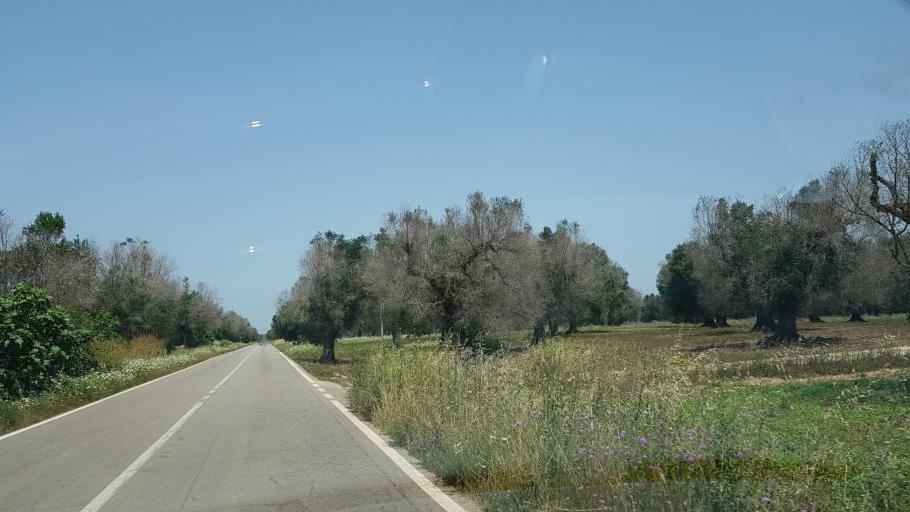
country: IT
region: Apulia
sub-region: Provincia di Lecce
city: Veglie
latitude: 40.3118
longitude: 17.9208
